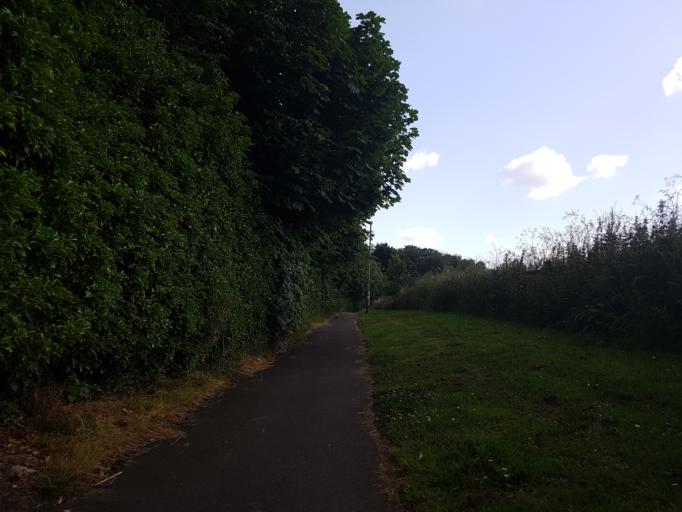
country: GB
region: England
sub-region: Northumberland
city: Alnmouth
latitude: 55.3959
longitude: -1.6338
